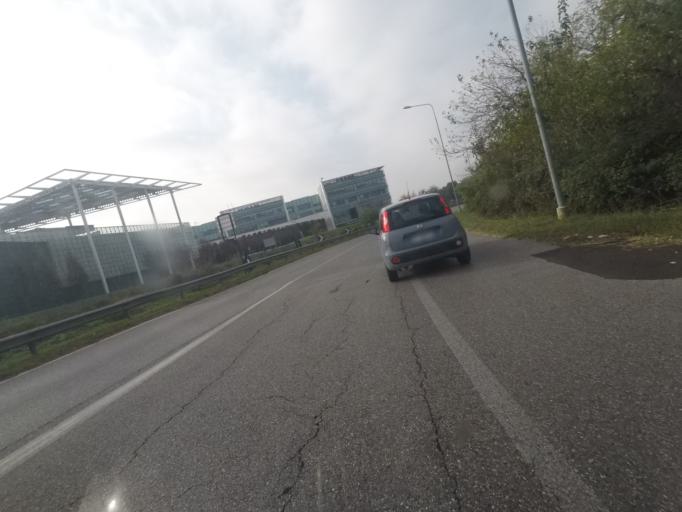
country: IT
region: Lombardy
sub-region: Provincia di Monza e Brianza
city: Vimercate
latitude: 45.5999
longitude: 9.3555
